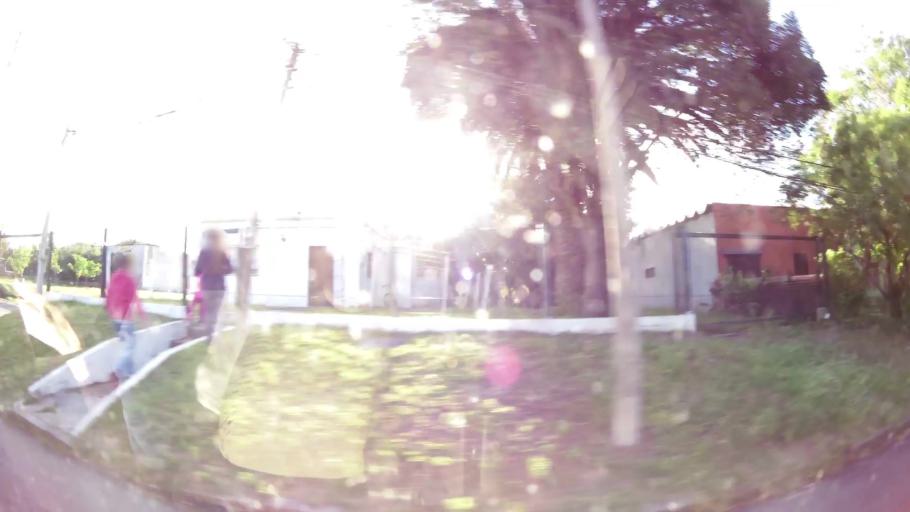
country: UY
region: Montevideo
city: Montevideo
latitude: -34.8785
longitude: -56.2659
